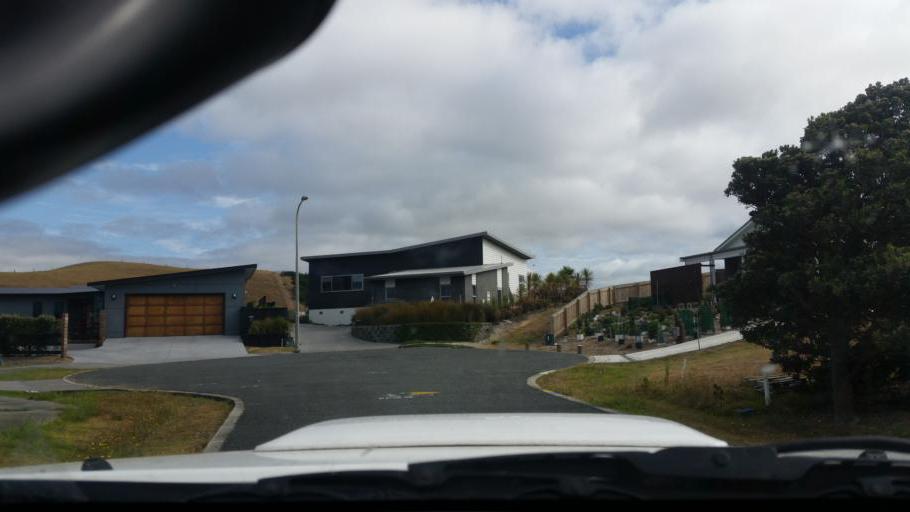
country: NZ
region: Northland
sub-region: Kaipara District
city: Dargaville
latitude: -35.9482
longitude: 173.7437
